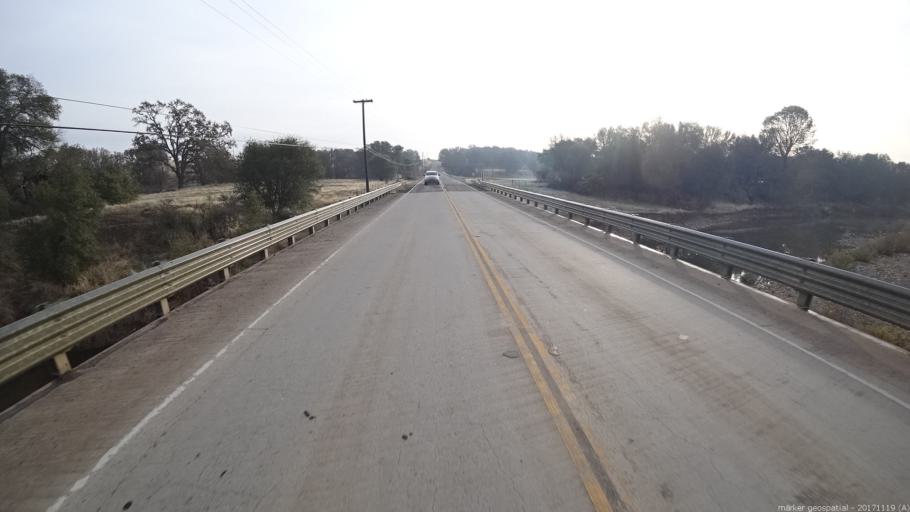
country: US
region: California
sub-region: Shasta County
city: Anderson
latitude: 40.4799
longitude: -122.2590
